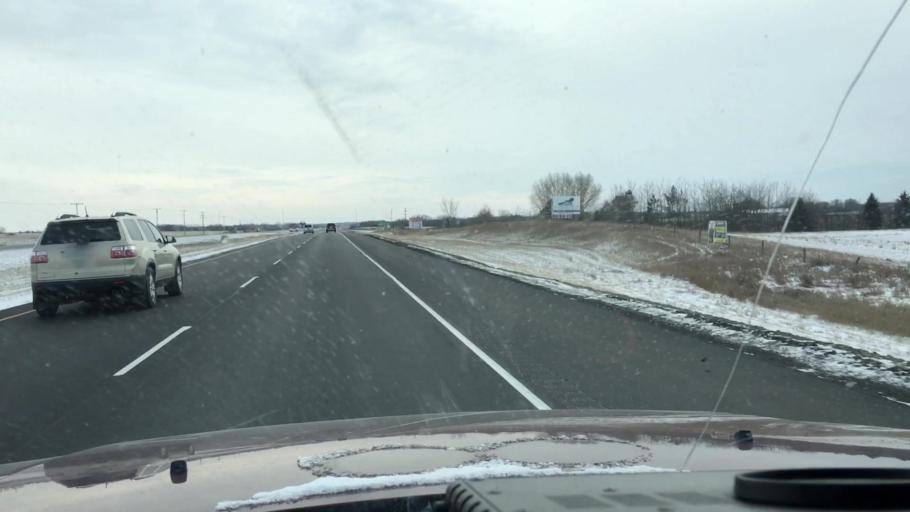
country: CA
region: Saskatchewan
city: Saskatoon
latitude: 52.0307
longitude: -106.5842
